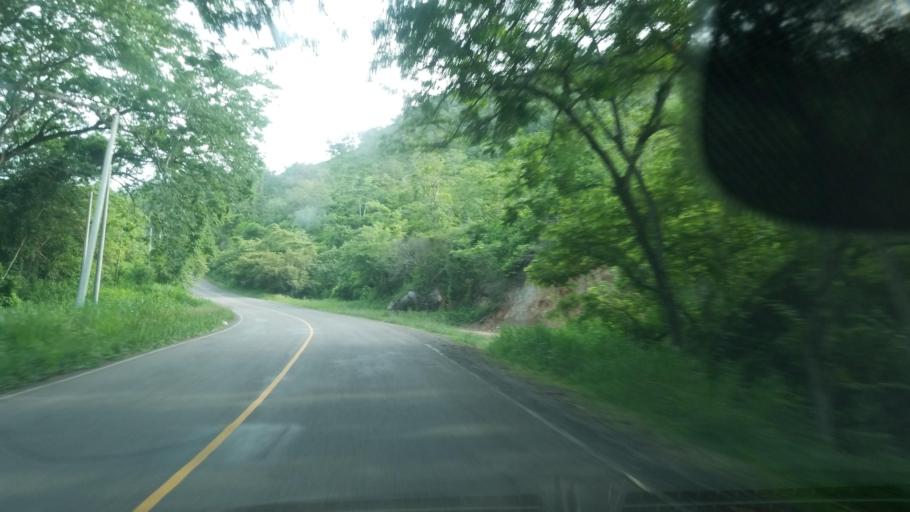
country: HN
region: Santa Barbara
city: Ilama
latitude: 15.0988
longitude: -88.2038
